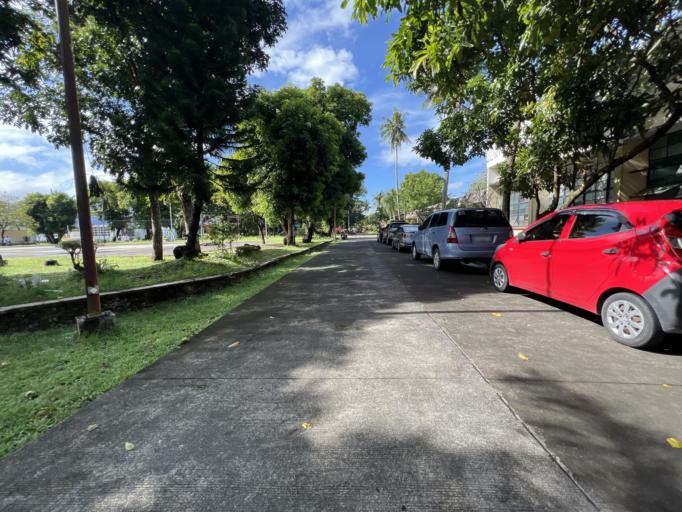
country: PH
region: Bicol
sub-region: Province of Albay
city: Sagpon
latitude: 13.1483
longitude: 123.7293
